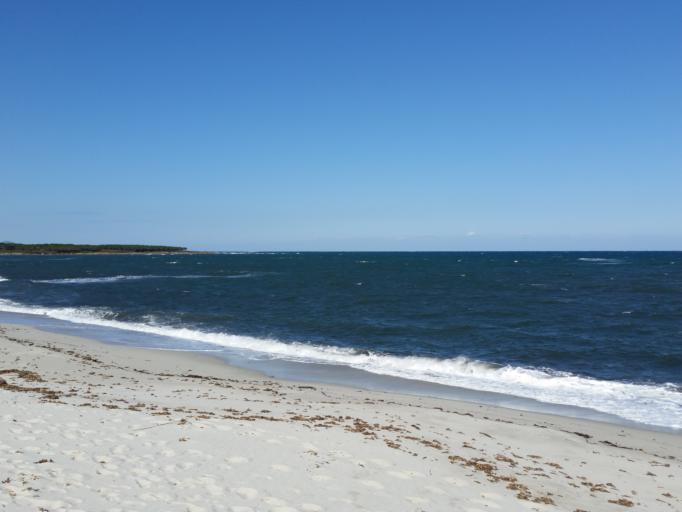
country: IT
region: Sardinia
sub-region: Provincia di Olbia-Tempio
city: Budoni
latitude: 40.7173
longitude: 9.7135
